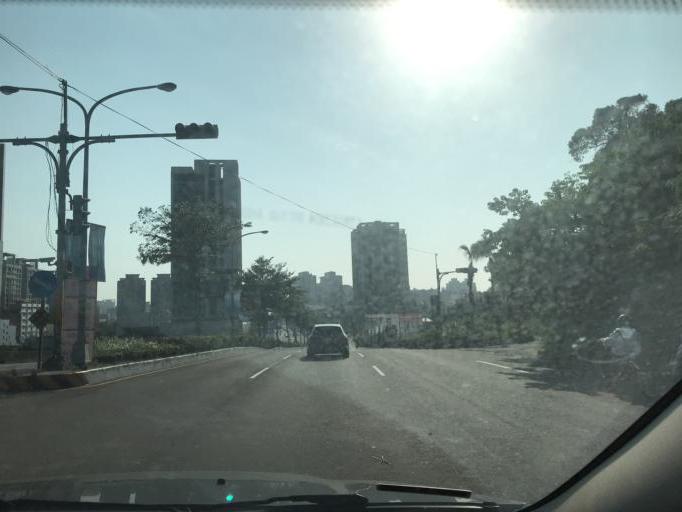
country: TW
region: Taiwan
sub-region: Hsinchu
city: Zhubei
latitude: 24.8281
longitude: 121.0353
